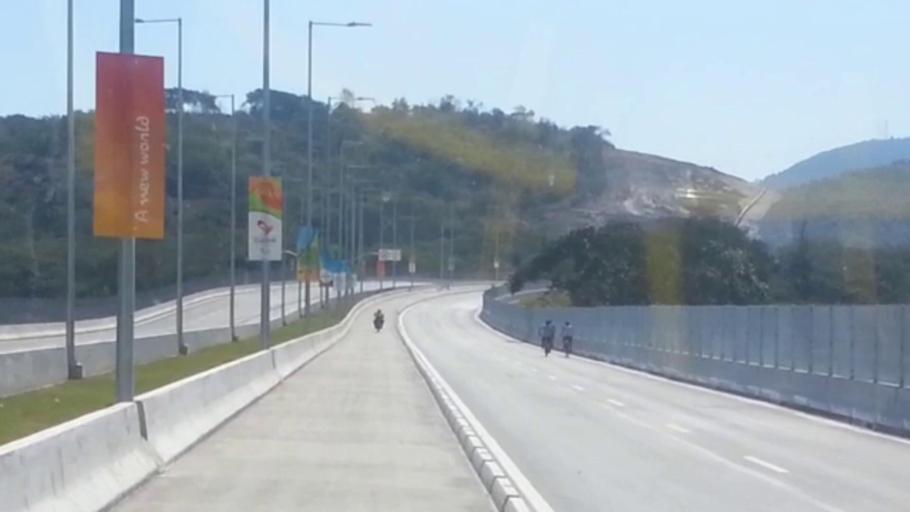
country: BR
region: Rio de Janeiro
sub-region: Nilopolis
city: Nilopolis
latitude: -22.9369
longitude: -43.3952
